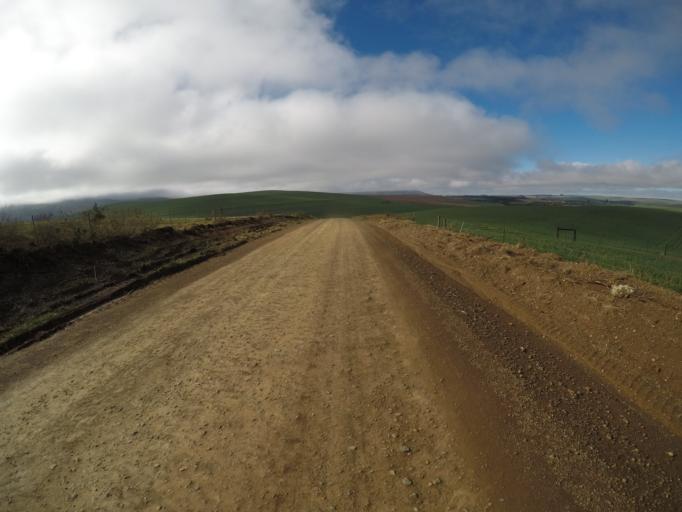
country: ZA
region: Western Cape
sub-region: Overberg District Municipality
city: Caledon
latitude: -34.1095
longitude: 19.7643
